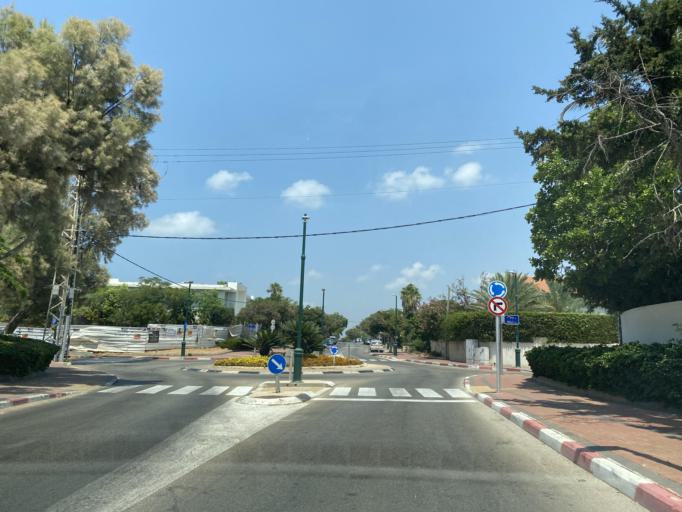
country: IL
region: Tel Aviv
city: Herzliya Pituah
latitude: 32.1751
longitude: 34.8041
